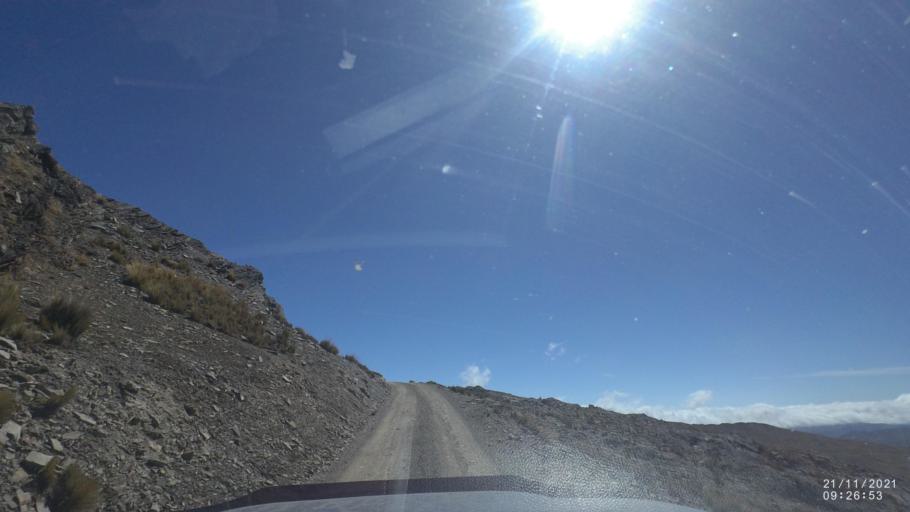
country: BO
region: Cochabamba
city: Cochabamba
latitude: -17.0856
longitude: -66.2525
